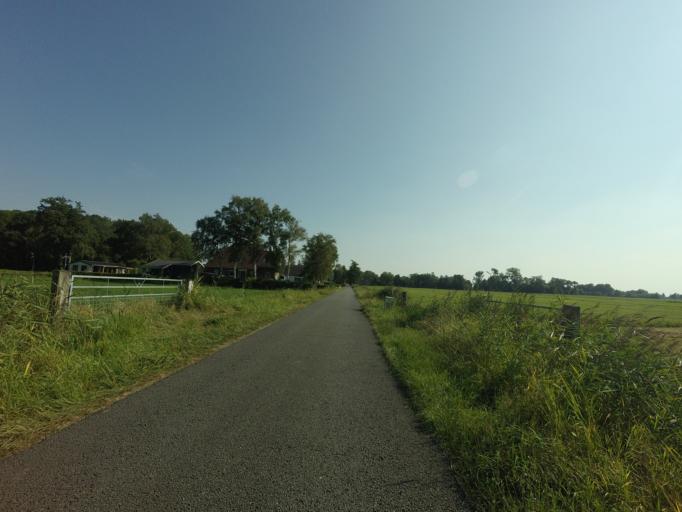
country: NL
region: Groningen
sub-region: Gemeente Zuidhorn
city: Zuidhorn
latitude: 53.2059
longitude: 6.4375
